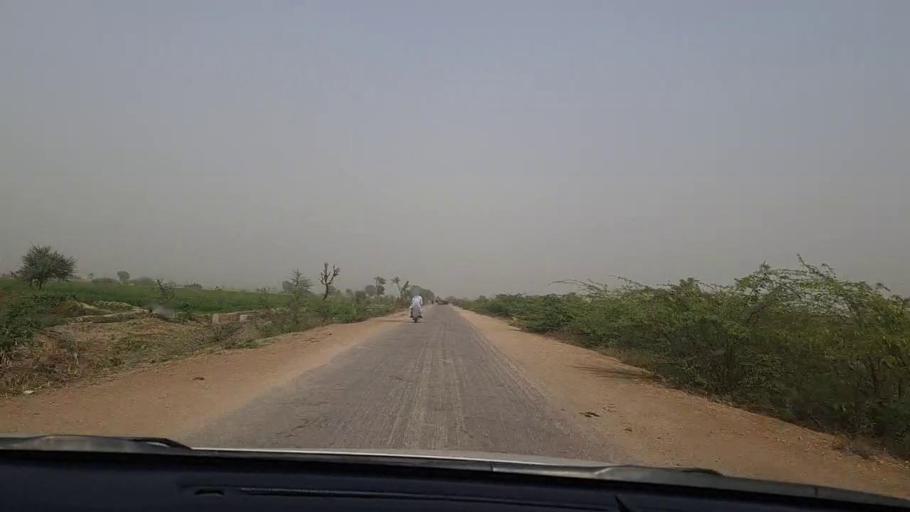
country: PK
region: Sindh
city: Samaro
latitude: 25.3936
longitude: 69.3733
